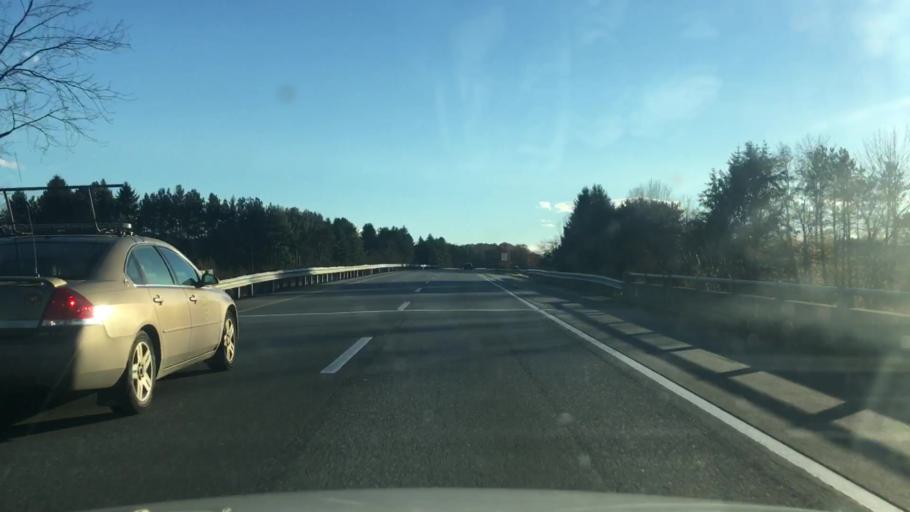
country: US
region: Maine
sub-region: Somerset County
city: Pittsfield
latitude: 44.7694
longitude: -69.4113
